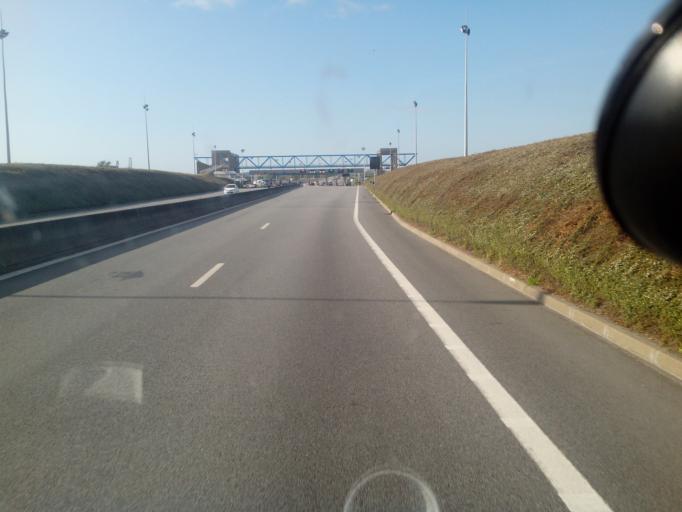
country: FR
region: Lower Normandy
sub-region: Departement du Calvados
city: La Riviere-Saint-Sauveur
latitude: 49.4471
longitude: 0.2720
